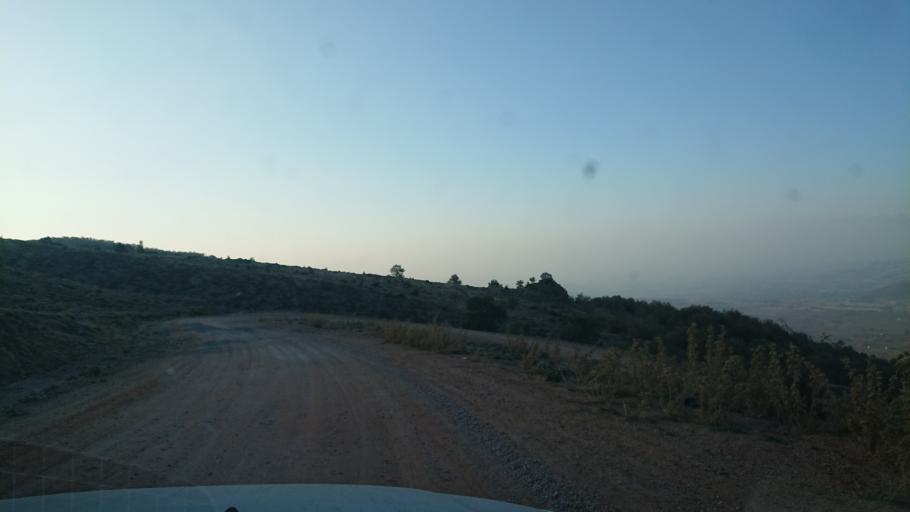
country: TR
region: Aksaray
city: Taspinar
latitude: 38.1675
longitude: 34.1803
